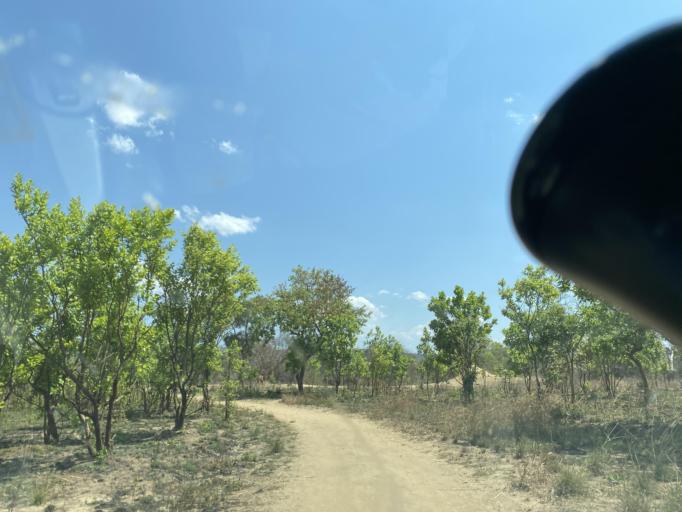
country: ZM
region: Lusaka
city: Chongwe
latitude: -15.0831
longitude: 29.4999
